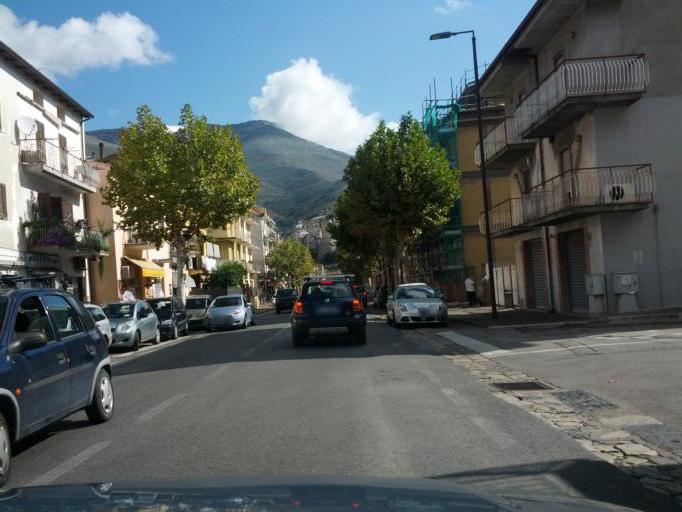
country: IT
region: Latium
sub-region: Provincia di Latina
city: Itri
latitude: 41.2899
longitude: 13.5244
